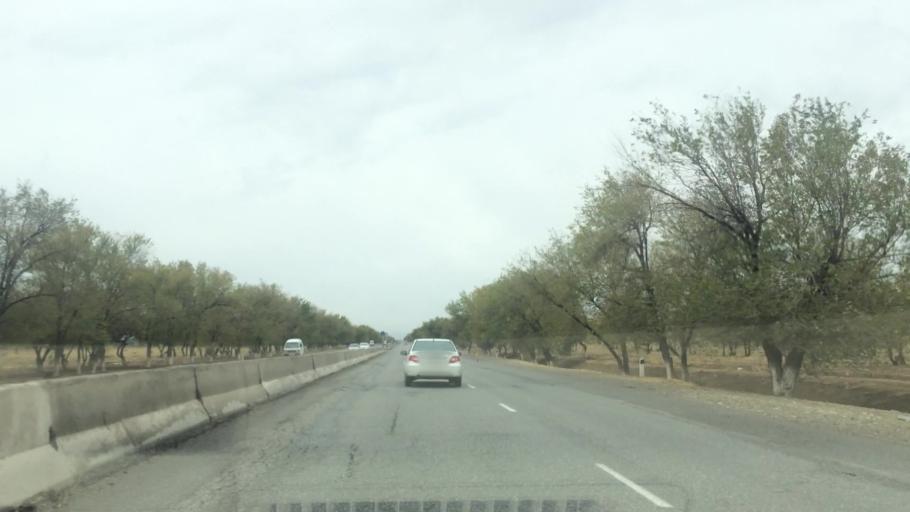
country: UZ
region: Samarqand
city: Bulung'ur
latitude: 39.8126
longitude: 67.3707
